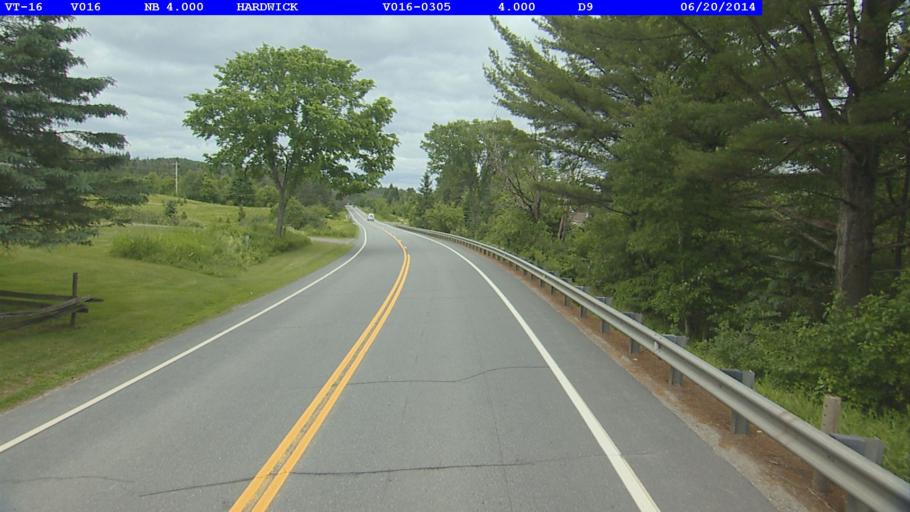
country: US
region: Vermont
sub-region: Caledonia County
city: Hardwick
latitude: 44.5387
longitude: -72.2708
